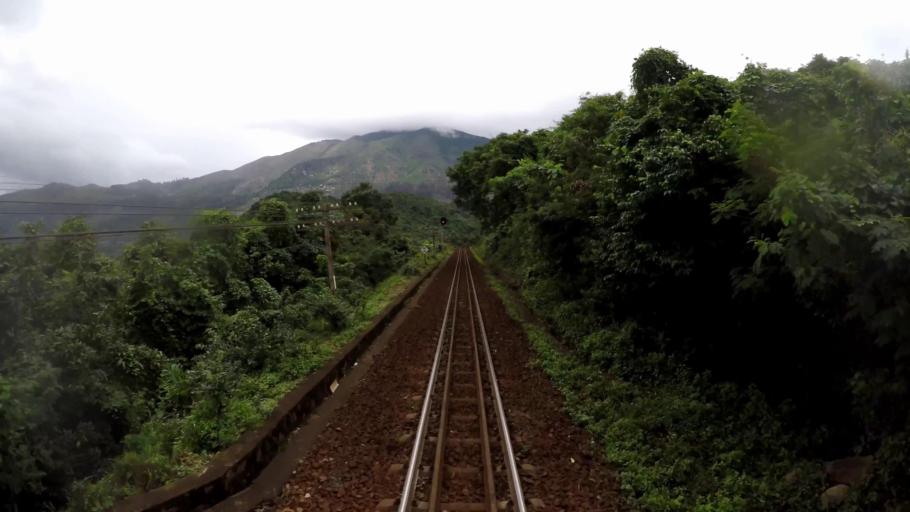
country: VN
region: Da Nang
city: Lien Chieu
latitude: 16.1706
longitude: 108.1470
